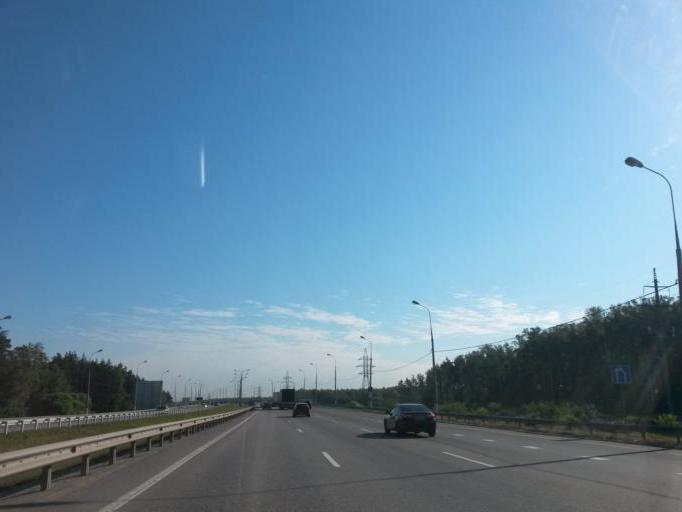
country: RU
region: Moskovskaya
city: Vostryakovo
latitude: 55.4089
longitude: 37.7889
